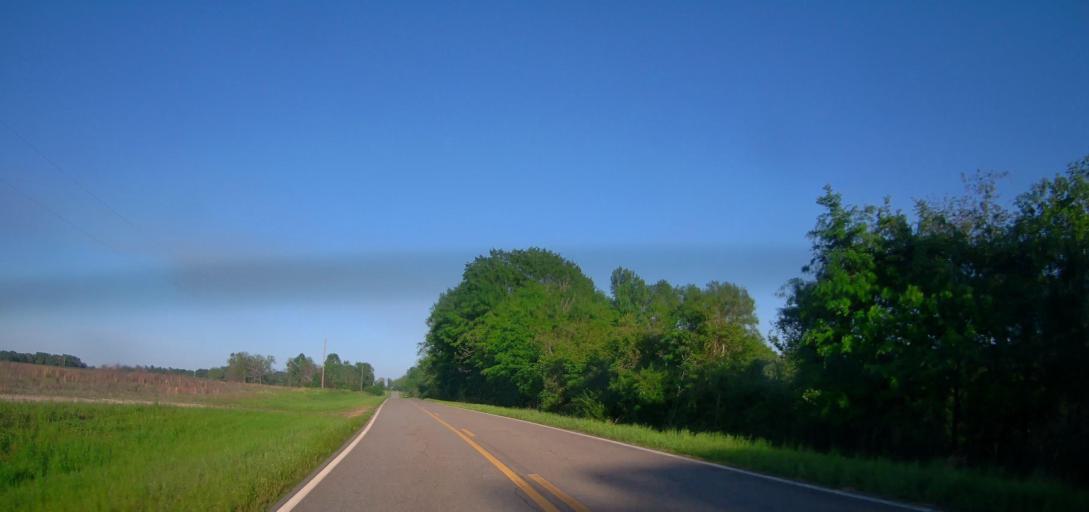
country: US
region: Georgia
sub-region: Macon County
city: Oglethorpe
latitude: 32.3019
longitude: -84.1002
